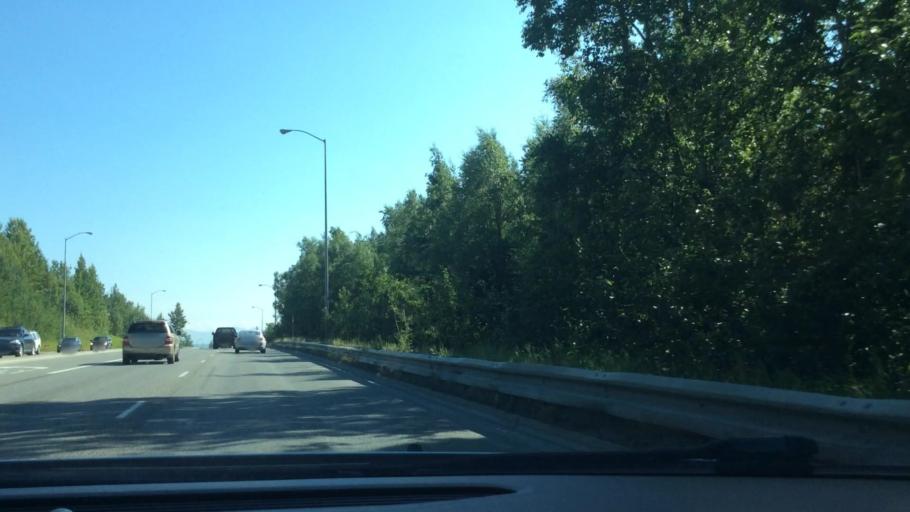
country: US
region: Alaska
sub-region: Anchorage Municipality
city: Anchorage
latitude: 61.2061
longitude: -149.7786
